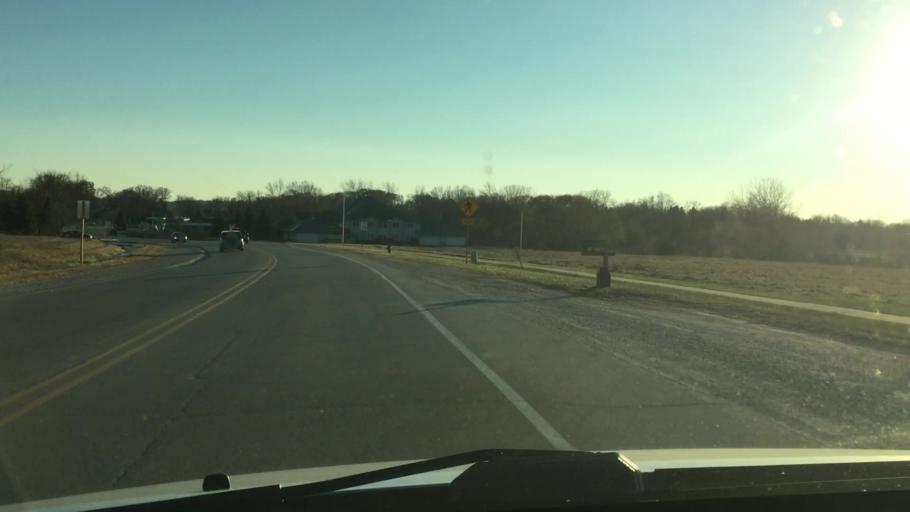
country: US
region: Wisconsin
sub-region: Waukesha County
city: Pewaukee
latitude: 43.0925
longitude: -88.2746
